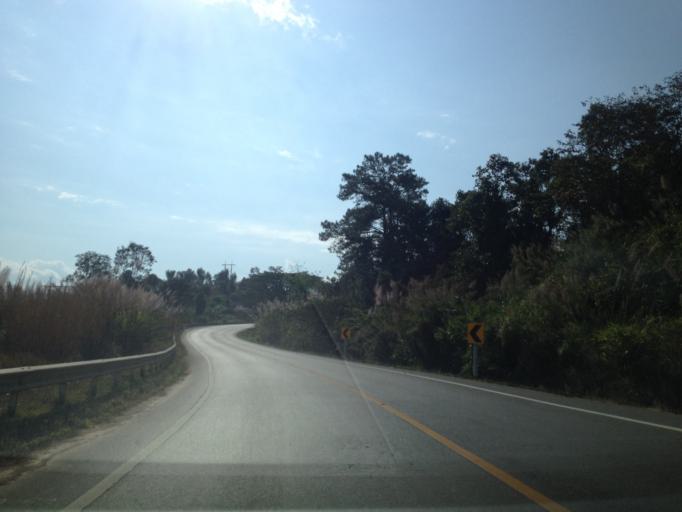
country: TH
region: Mae Hong Son
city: Pa Pae
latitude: 18.1636
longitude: 98.2329
